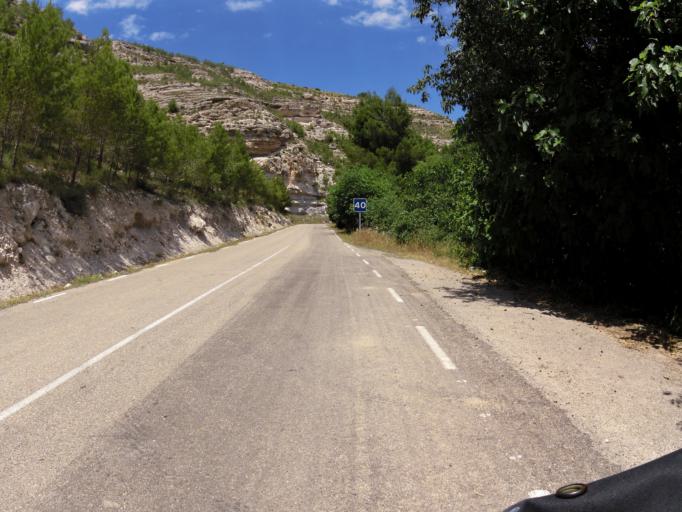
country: ES
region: Castille-La Mancha
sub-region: Provincia de Albacete
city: Jorquera
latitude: 39.1700
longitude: -1.5432
